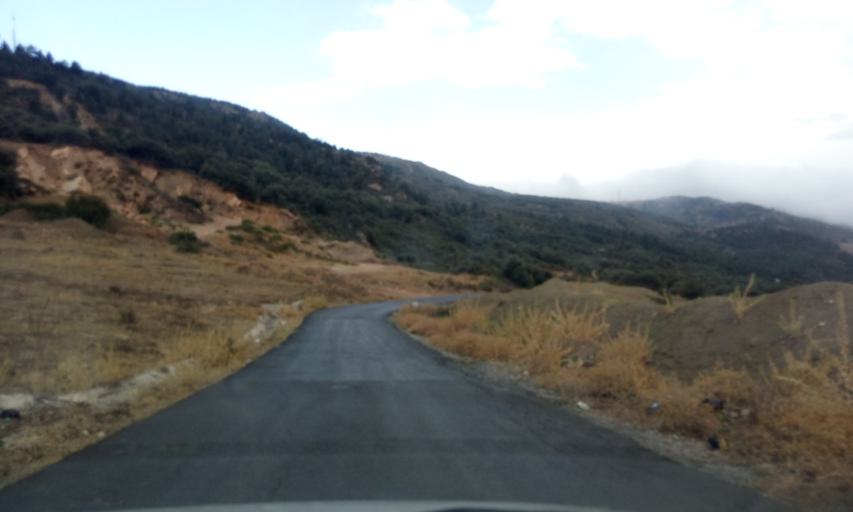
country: DZ
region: Tizi Ouzou
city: Chemini
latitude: 36.6142
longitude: 4.5574
